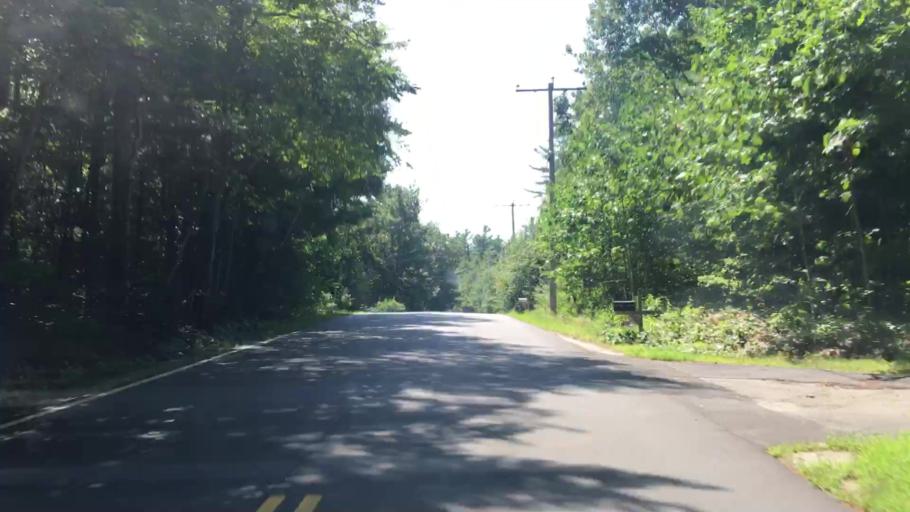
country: US
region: New Hampshire
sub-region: Rockingham County
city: Hampstead
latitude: 42.8946
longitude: -71.2163
